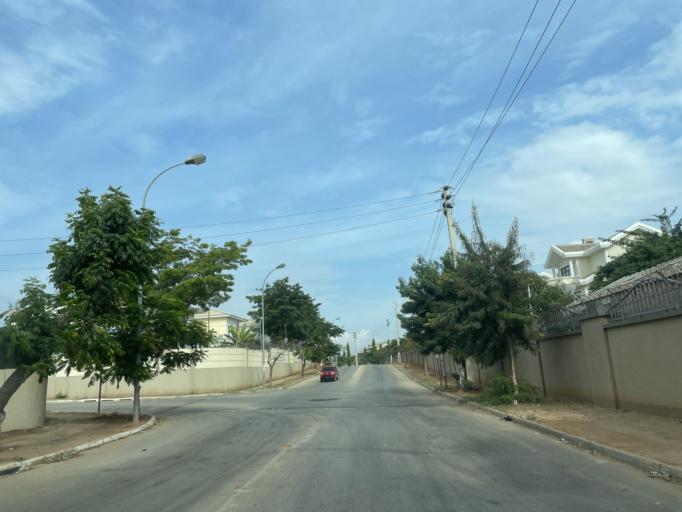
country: AO
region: Luanda
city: Luanda
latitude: -8.9313
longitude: 13.1828
